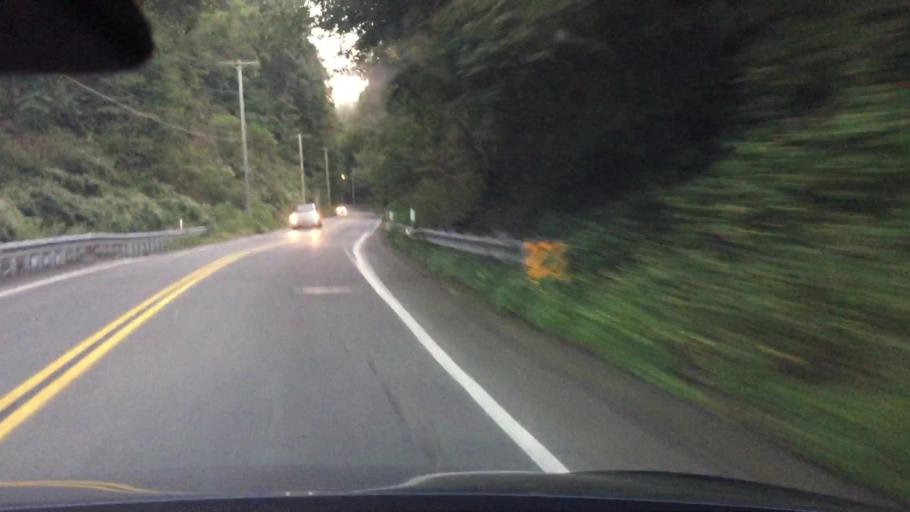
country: US
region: Pennsylvania
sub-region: Allegheny County
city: Blawnox
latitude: 40.4805
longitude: -79.8754
